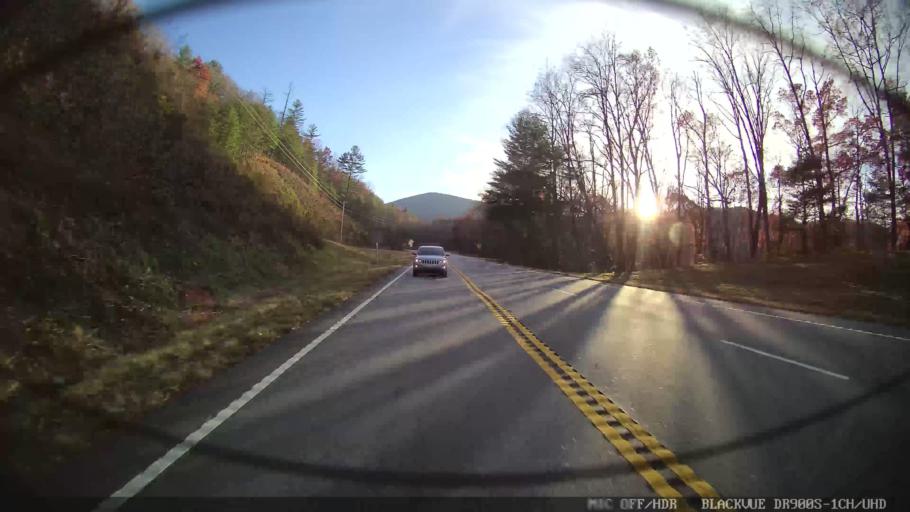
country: US
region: Georgia
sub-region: Union County
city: Blairsville
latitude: 34.7651
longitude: -83.9217
